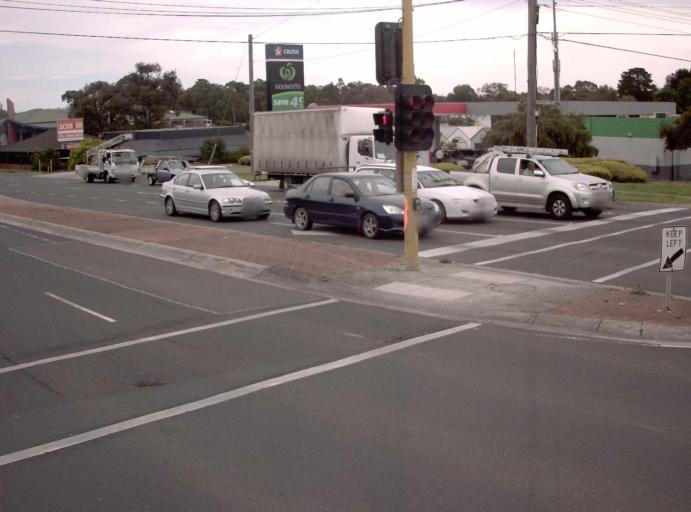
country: AU
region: Victoria
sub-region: Knox
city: Wantirna
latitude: -37.8477
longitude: 145.2270
